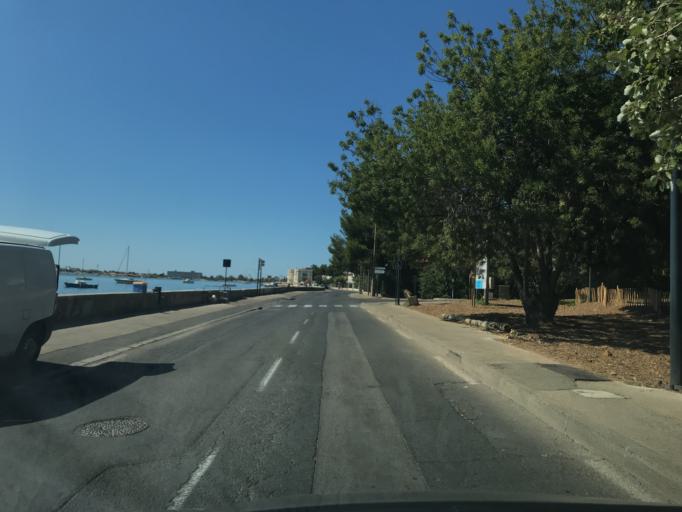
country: FR
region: Provence-Alpes-Cote d'Azur
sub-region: Departement du Var
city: La Seyne-sur-Mer
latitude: 43.0913
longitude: 5.9005
